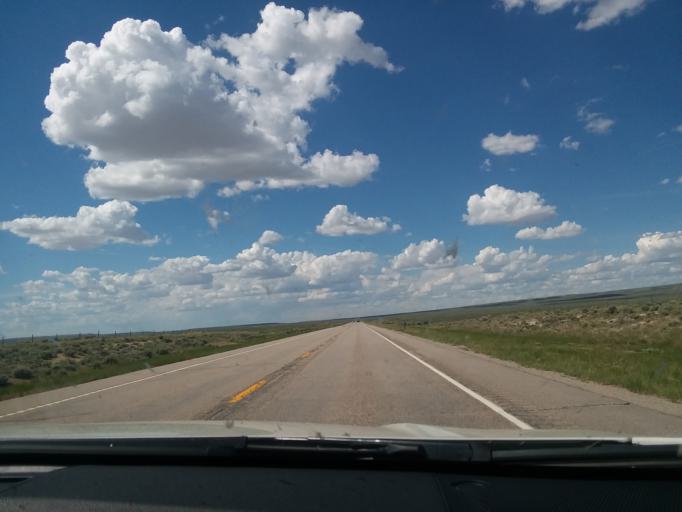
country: US
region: Wyoming
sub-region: Sweetwater County
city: North Rock Springs
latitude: 41.8022
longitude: -109.3353
